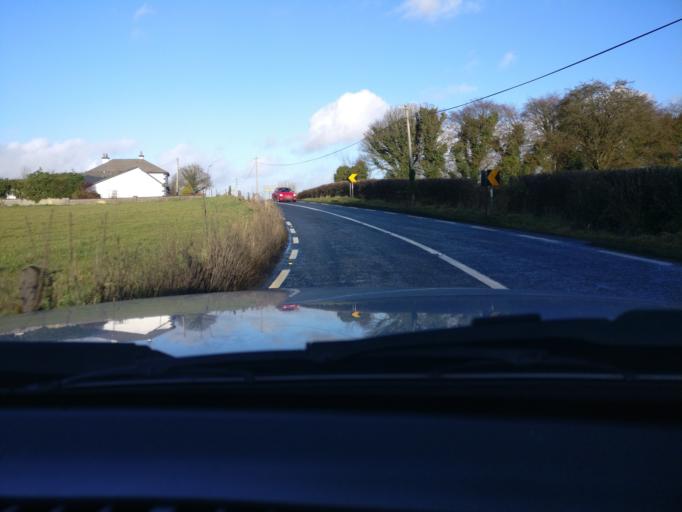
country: IE
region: Leinster
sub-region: An Iarmhi
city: Rathwire
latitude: 53.5682
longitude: -7.1903
